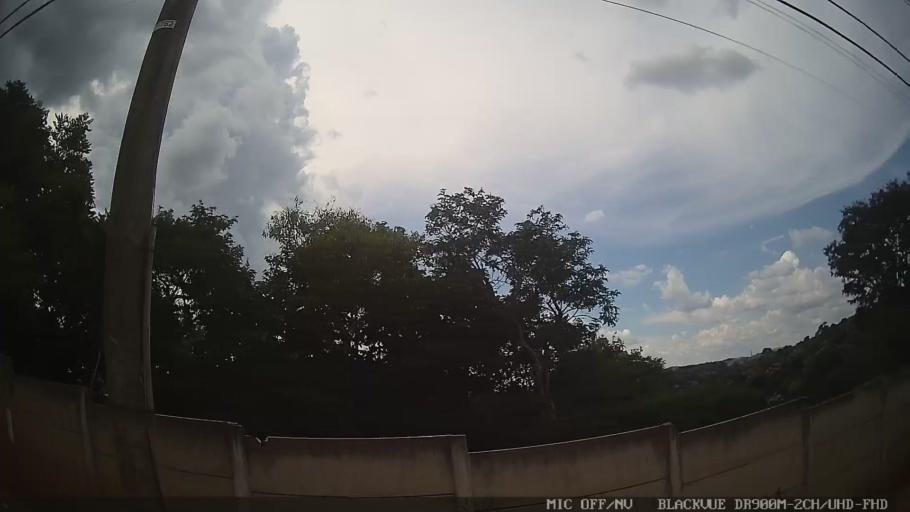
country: BR
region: Sao Paulo
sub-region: Atibaia
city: Atibaia
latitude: -23.1420
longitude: -46.5678
